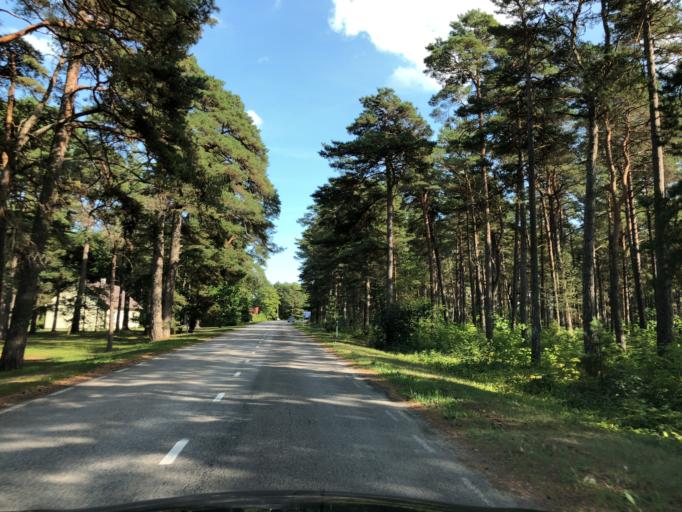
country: EE
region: Hiiumaa
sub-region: Kaerdla linn
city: Kardla
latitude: 58.7075
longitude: 22.5913
